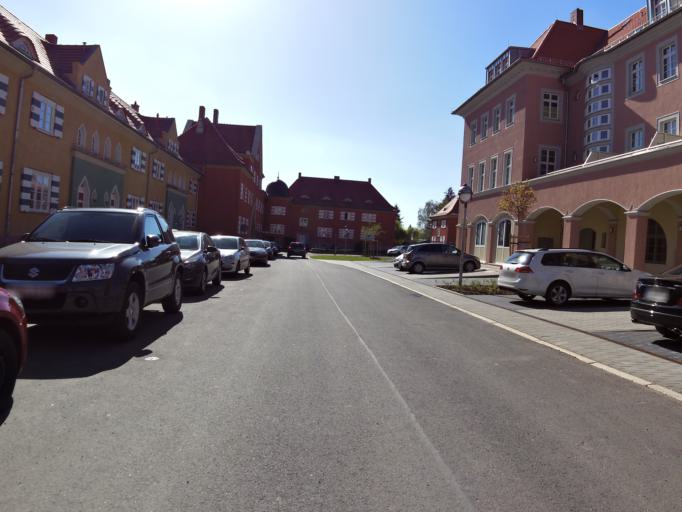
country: DE
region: Thuringia
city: Gotha
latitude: 50.9345
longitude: 10.6933
